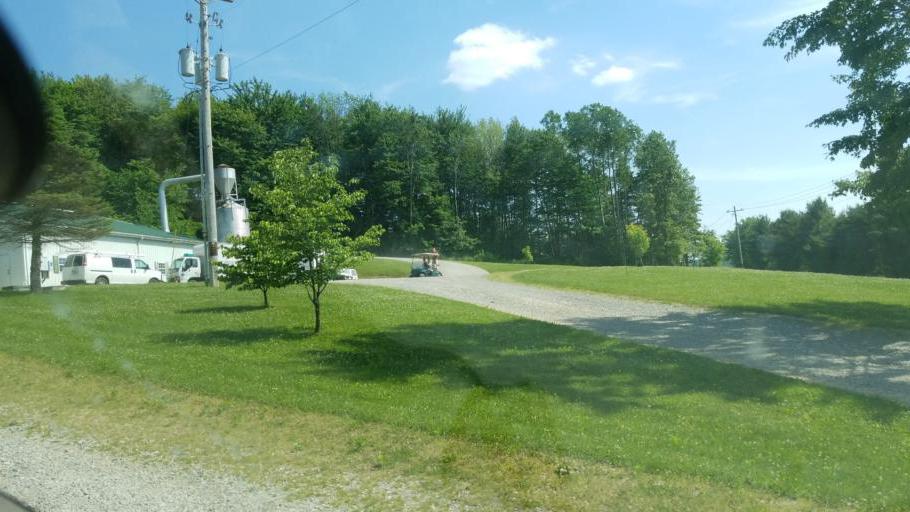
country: US
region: Ohio
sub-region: Knox County
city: Danville
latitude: 40.5180
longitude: -82.3614
